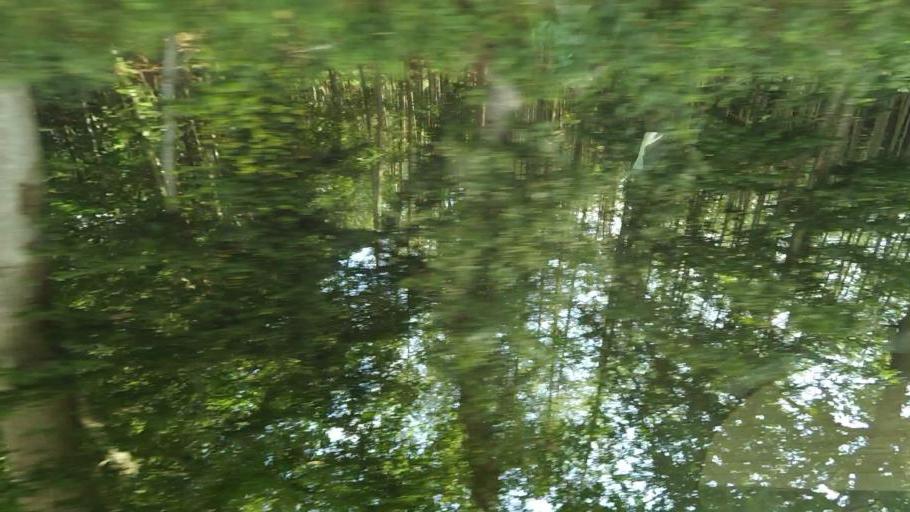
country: DK
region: Central Jutland
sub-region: Syddjurs Kommune
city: Ryomgard
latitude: 56.4642
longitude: 10.5232
